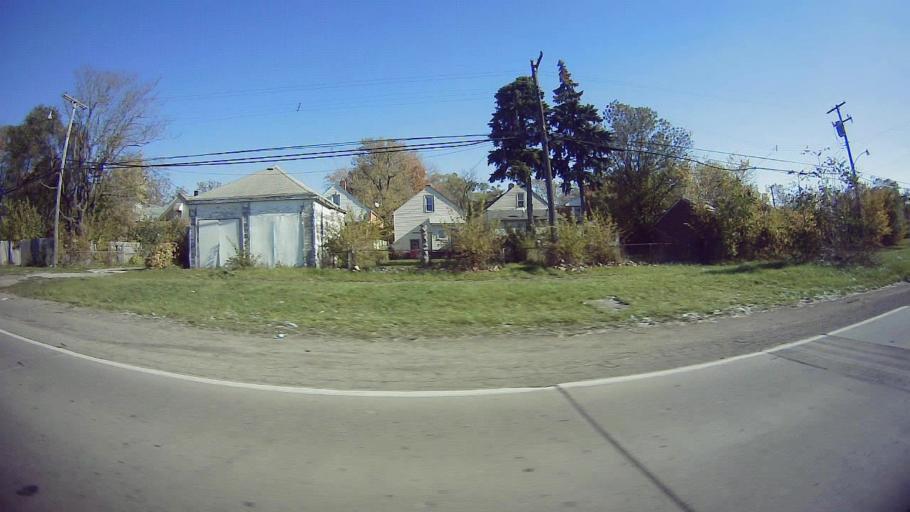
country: US
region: Michigan
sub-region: Wayne County
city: Hamtramck
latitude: 42.4118
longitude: -83.0424
